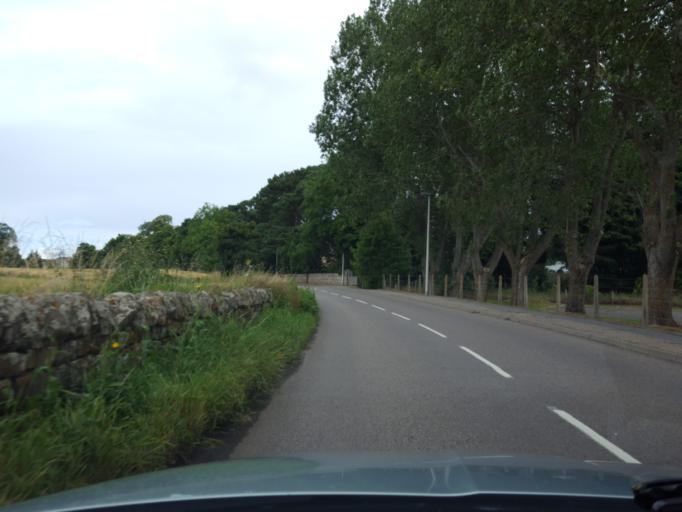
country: GB
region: Scotland
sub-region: Moray
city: Kinloss
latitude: 57.6339
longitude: -3.5617
